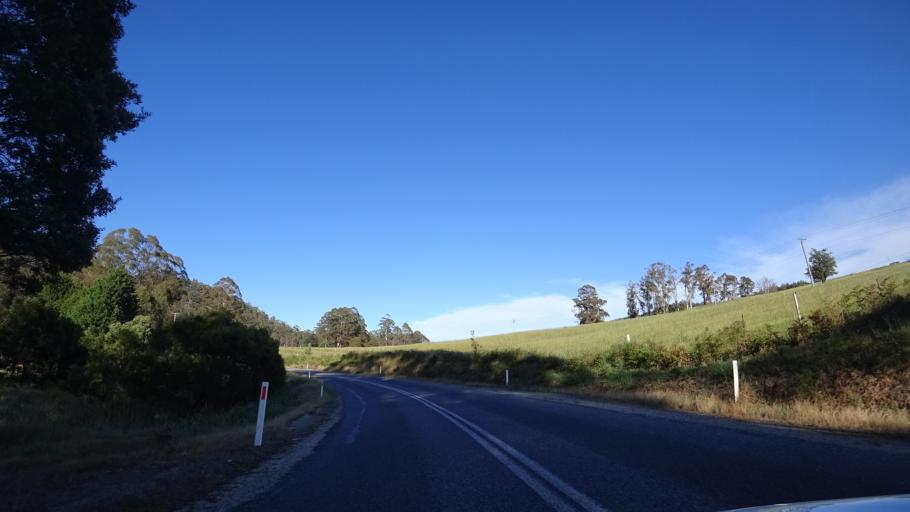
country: AU
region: Tasmania
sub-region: Break O'Day
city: St Helens
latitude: -41.2579
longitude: 148.0642
